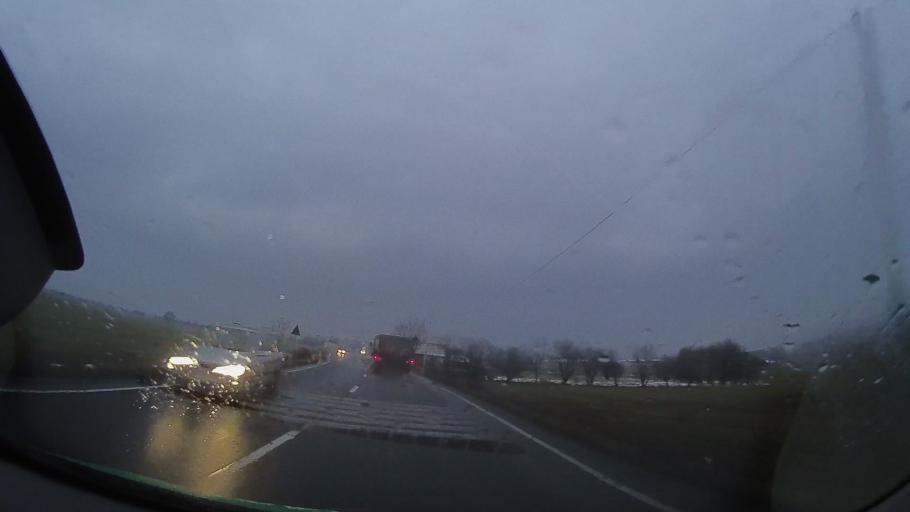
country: RO
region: Harghita
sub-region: Comuna Lazarea
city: Lazarea
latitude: 46.7597
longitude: 25.5162
